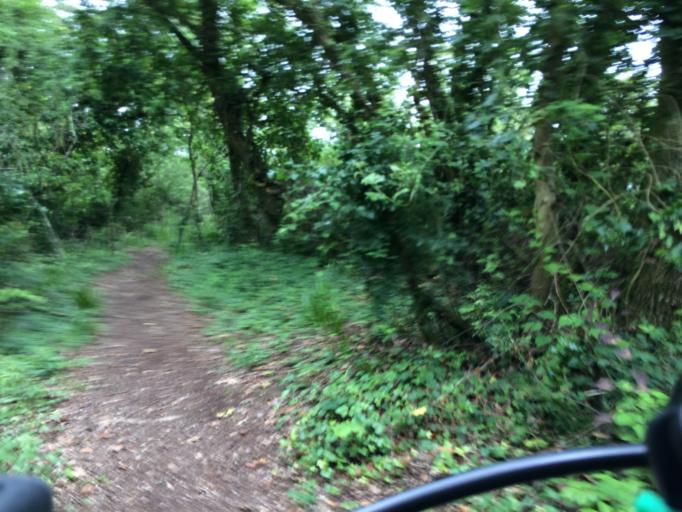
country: FR
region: Brittany
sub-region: Departement du Finistere
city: Hopital-Camfrout
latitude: 48.3272
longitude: -4.2550
